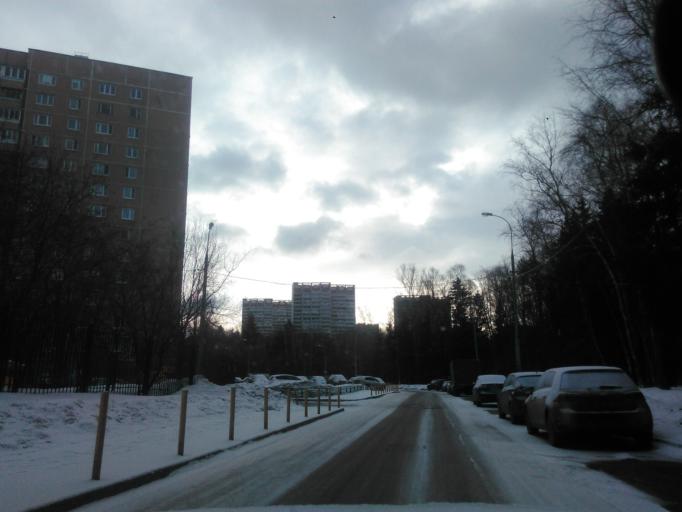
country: RU
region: Moscow
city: Zelenograd
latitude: 55.9951
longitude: 37.1788
